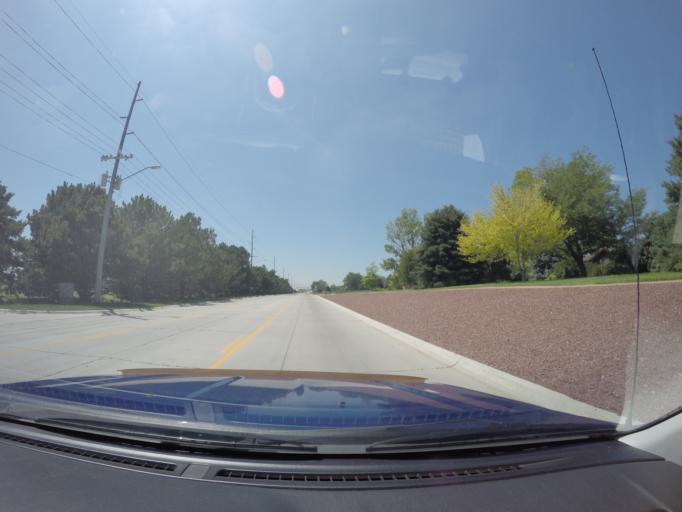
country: US
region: Nebraska
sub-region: Phelps County
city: Holdrege
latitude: 40.4525
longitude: -99.3754
